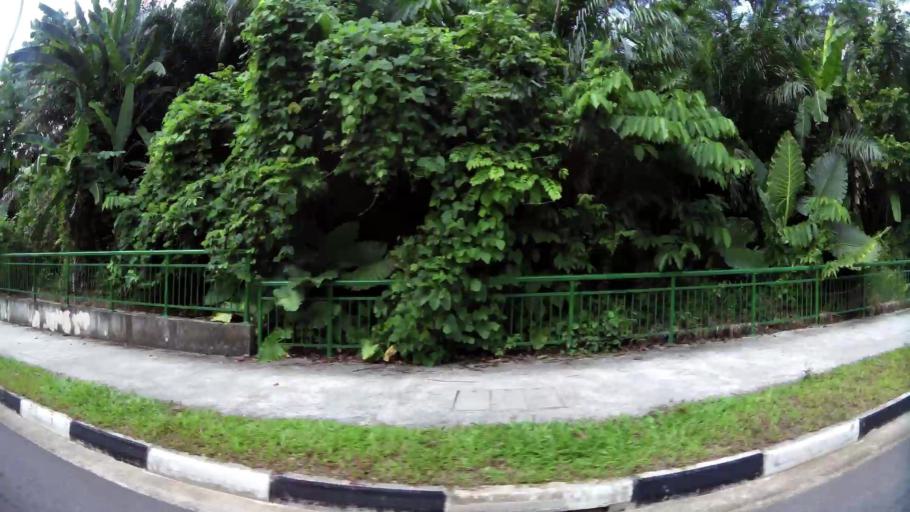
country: SG
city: Singapore
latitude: 1.3107
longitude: 103.8126
